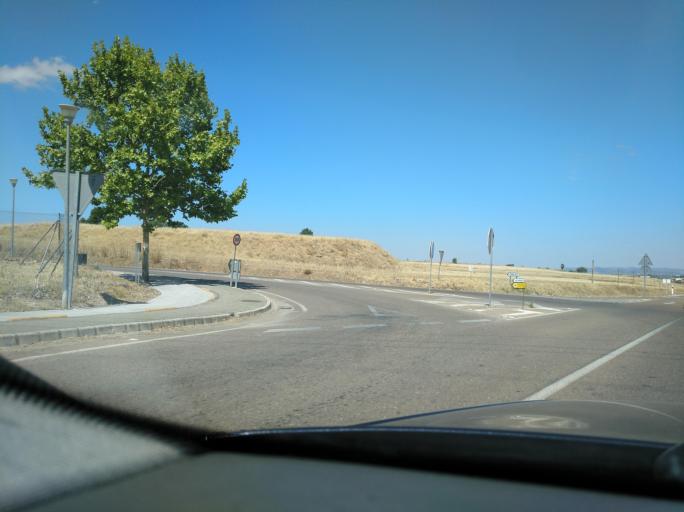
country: ES
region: Extremadura
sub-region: Provincia de Badajoz
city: Olivenza
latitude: 38.6926
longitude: -7.1005
